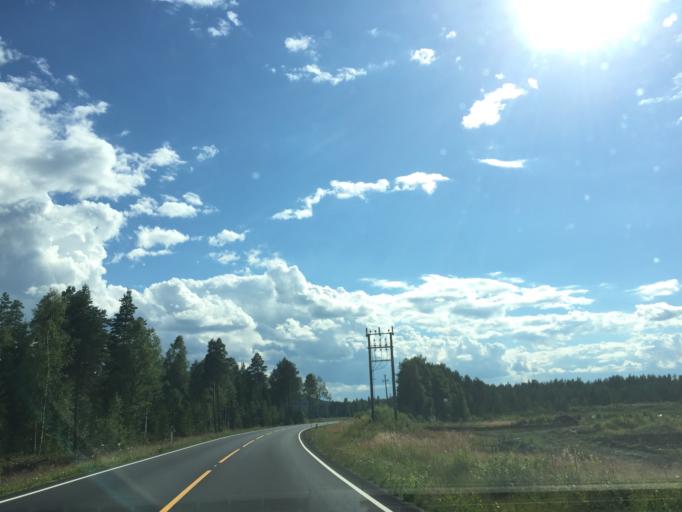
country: NO
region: Hedmark
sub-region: Sor-Odal
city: Skarnes
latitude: 60.1912
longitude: 11.6068
